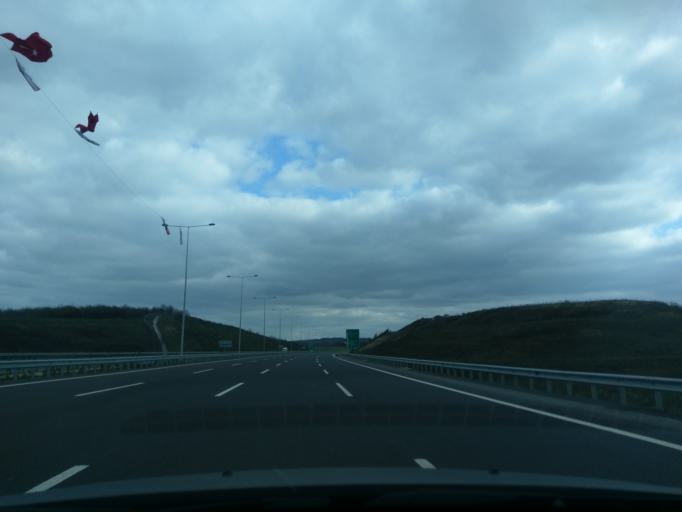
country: TR
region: Istanbul
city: Kemerburgaz
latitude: 41.2379
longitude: 28.8243
